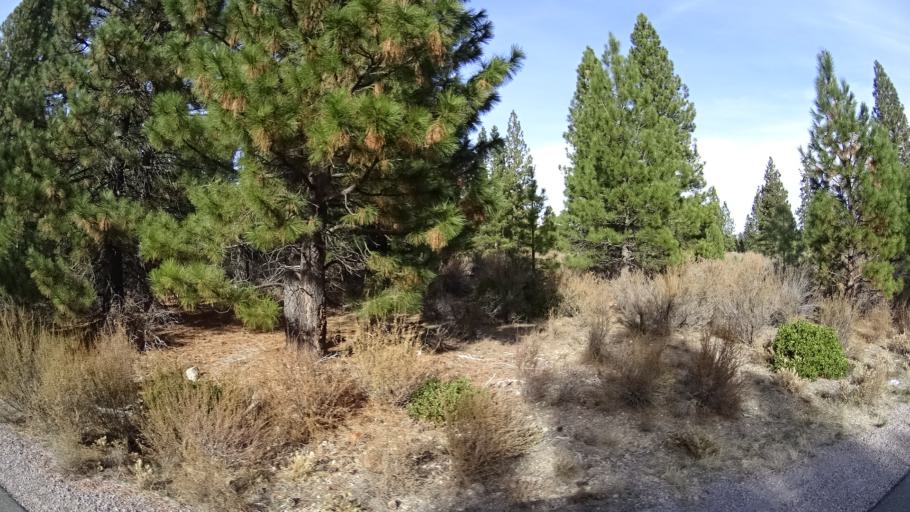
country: US
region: California
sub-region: Siskiyou County
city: Weed
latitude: 41.3941
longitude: -122.3846
